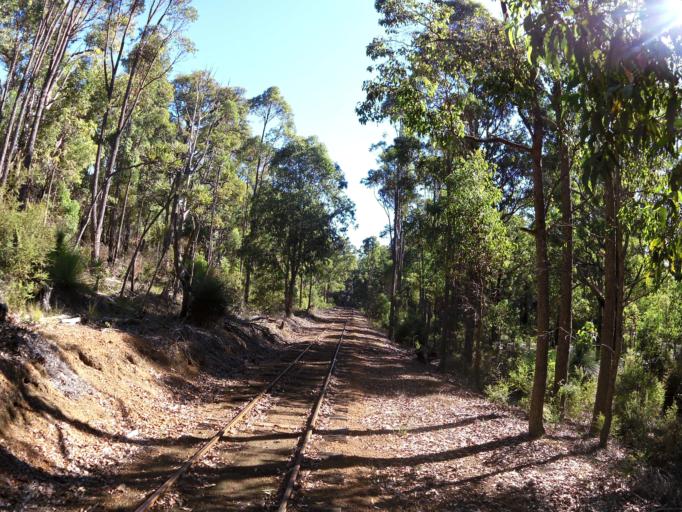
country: AU
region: Western Australia
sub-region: Waroona
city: Waroona
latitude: -32.7100
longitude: 116.0806
